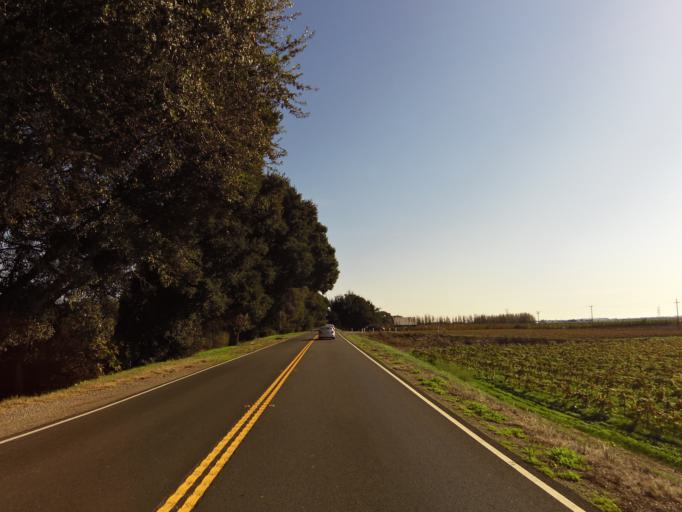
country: US
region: California
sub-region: Solano County
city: Rio Vista
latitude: 38.1682
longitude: -121.6355
